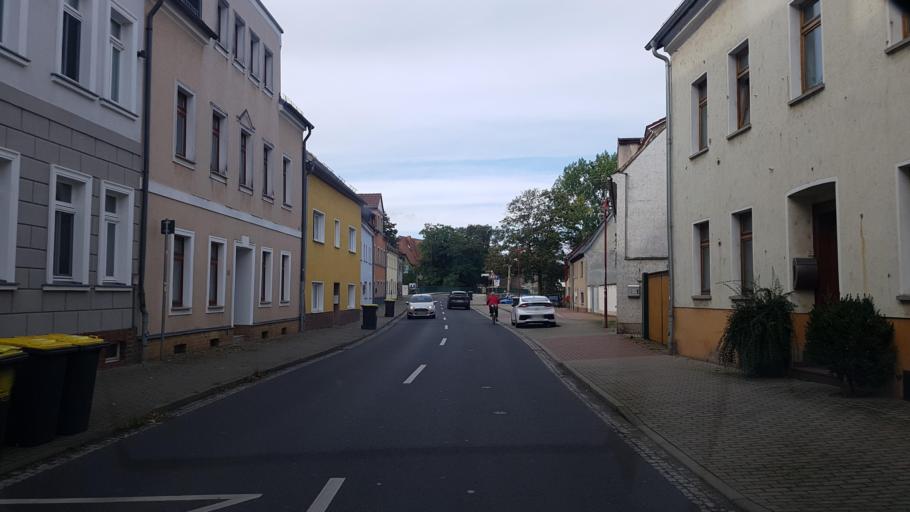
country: DE
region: Saxony
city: Pegau
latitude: 51.1656
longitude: 12.2628
